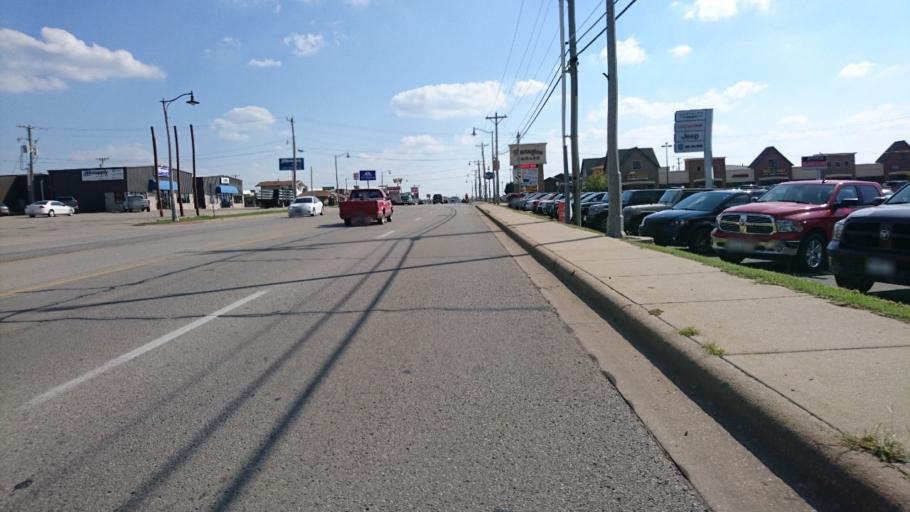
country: US
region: Missouri
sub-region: Laclede County
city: Lebanon
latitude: 37.6538
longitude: -92.6678
